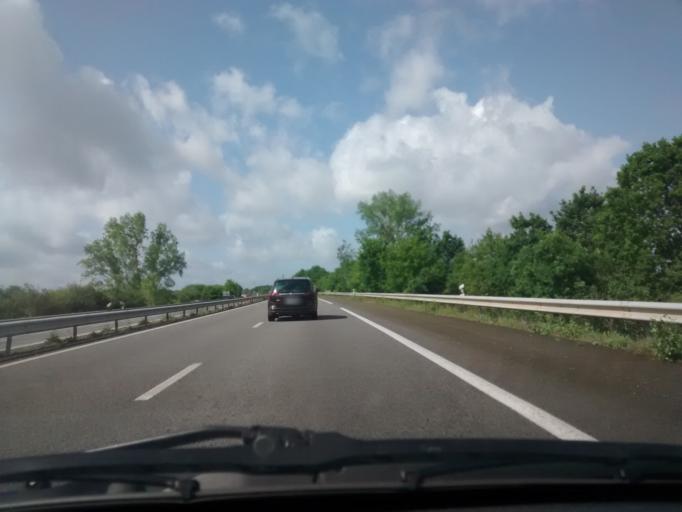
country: FR
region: Brittany
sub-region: Departement d'Ille-et-Vilaine
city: Le Rheu
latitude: 48.0893
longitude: -1.7789
